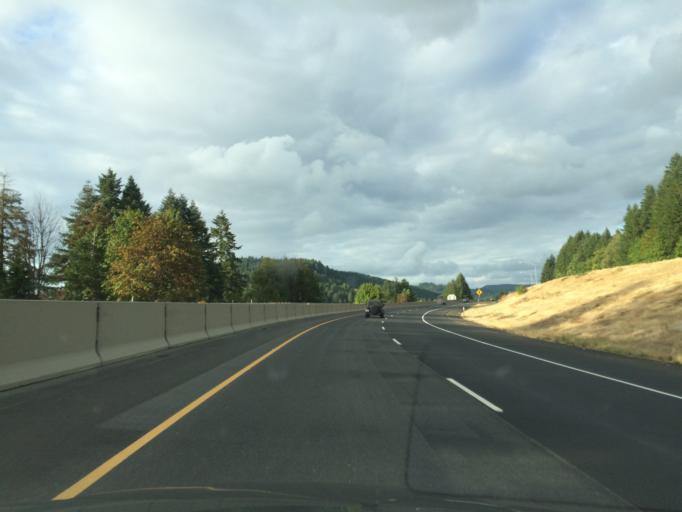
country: US
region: Oregon
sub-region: Douglas County
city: Drain
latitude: 43.7115
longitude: -123.2183
